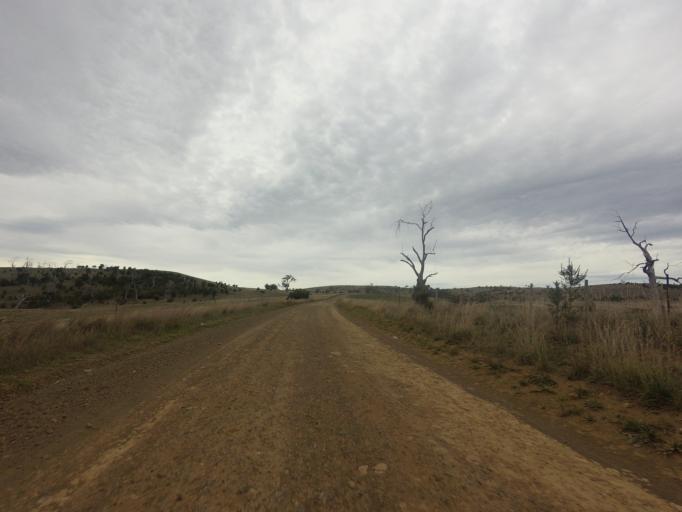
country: AU
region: Tasmania
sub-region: Derwent Valley
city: New Norfolk
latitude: -42.5572
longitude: 146.8819
